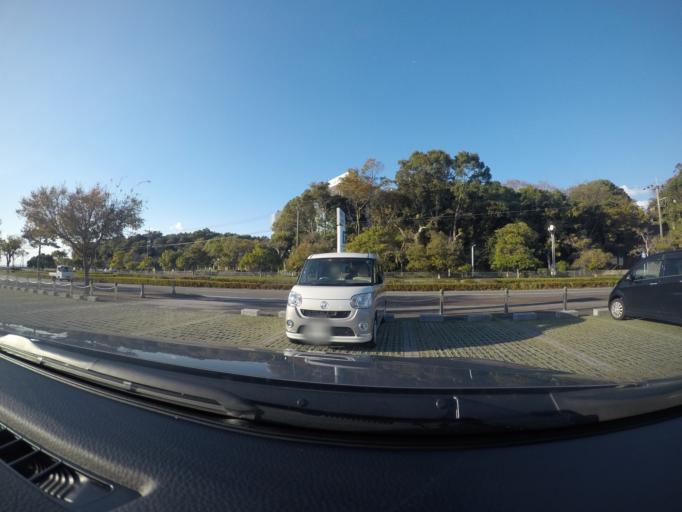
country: JP
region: Kumamoto
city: Minamata
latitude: 32.2027
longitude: 130.3747
